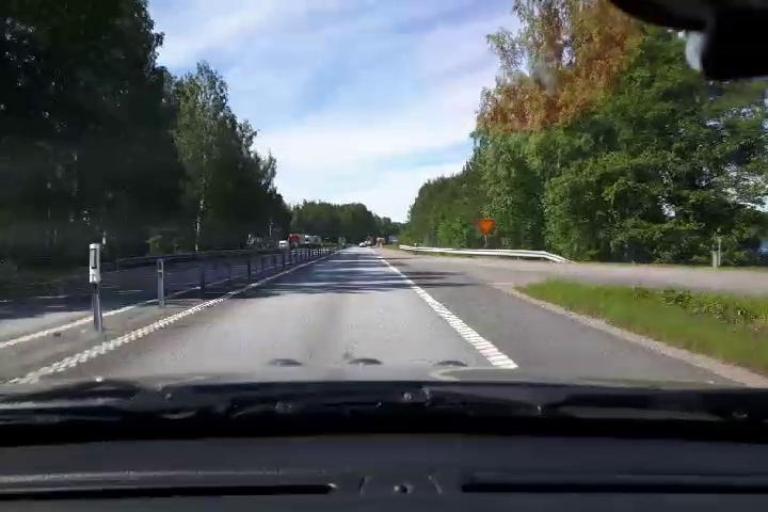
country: SE
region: Gaevleborg
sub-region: Gavle Kommun
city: Norrsundet
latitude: 61.0056
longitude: 16.9864
